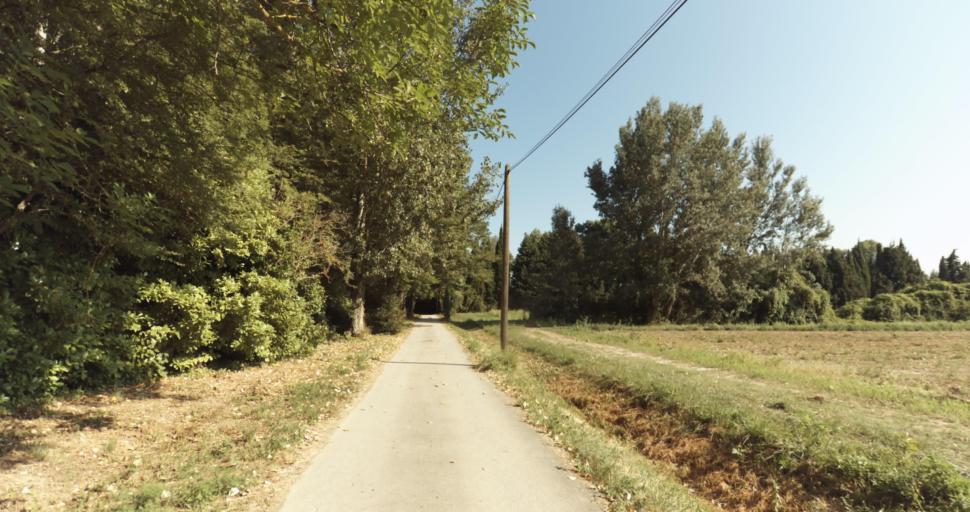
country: FR
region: Provence-Alpes-Cote d'Azur
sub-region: Departement du Vaucluse
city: Althen-des-Paluds
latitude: 44.0197
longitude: 4.9547
